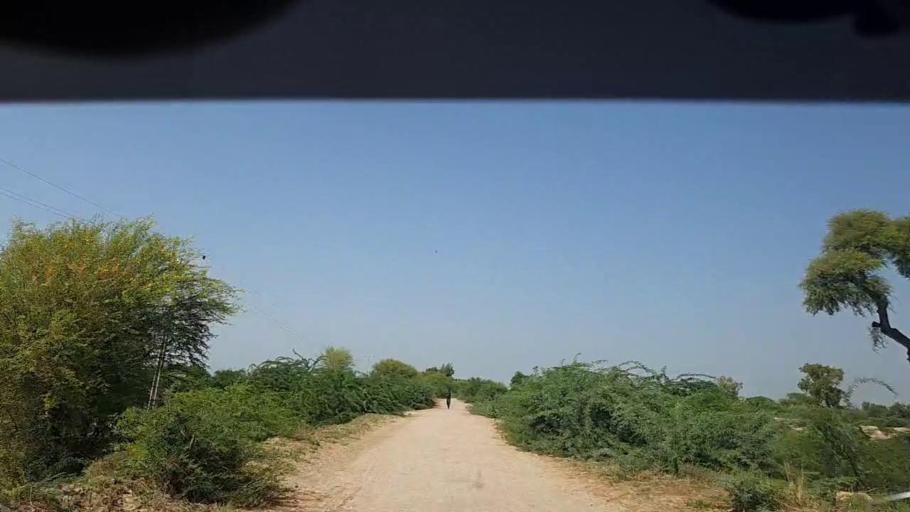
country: PK
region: Sindh
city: Badin
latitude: 24.4683
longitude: 68.7799
